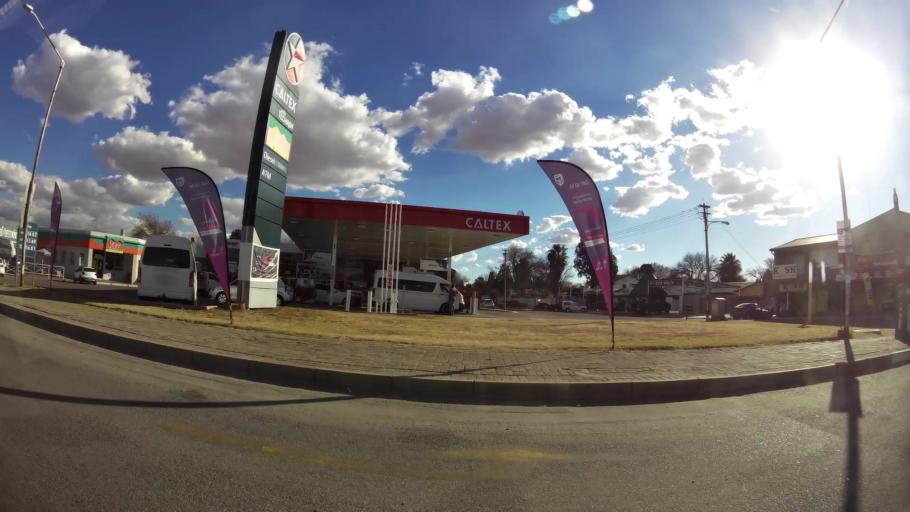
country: ZA
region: North-West
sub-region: Dr Kenneth Kaunda District Municipality
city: Klerksdorp
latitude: -26.8577
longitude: 26.6649
